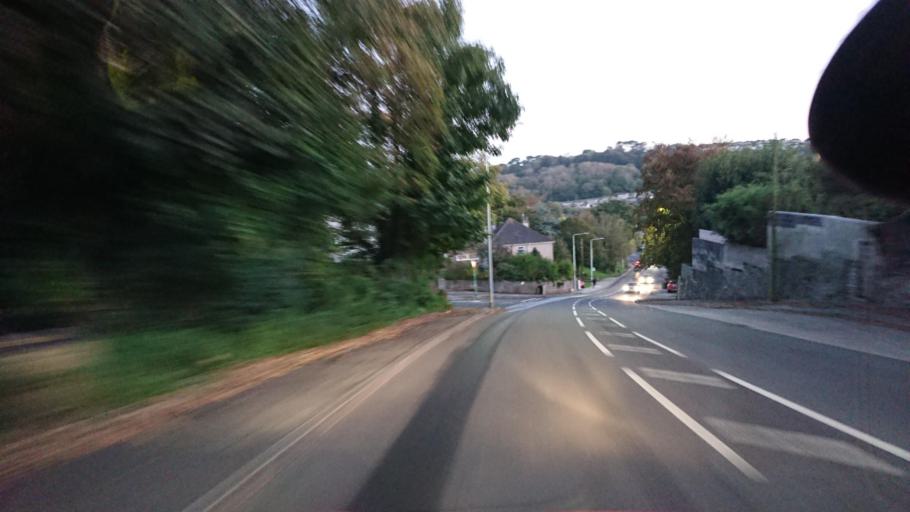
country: GB
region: England
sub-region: Plymouth
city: Plymouth
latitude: 50.4009
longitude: -4.1139
